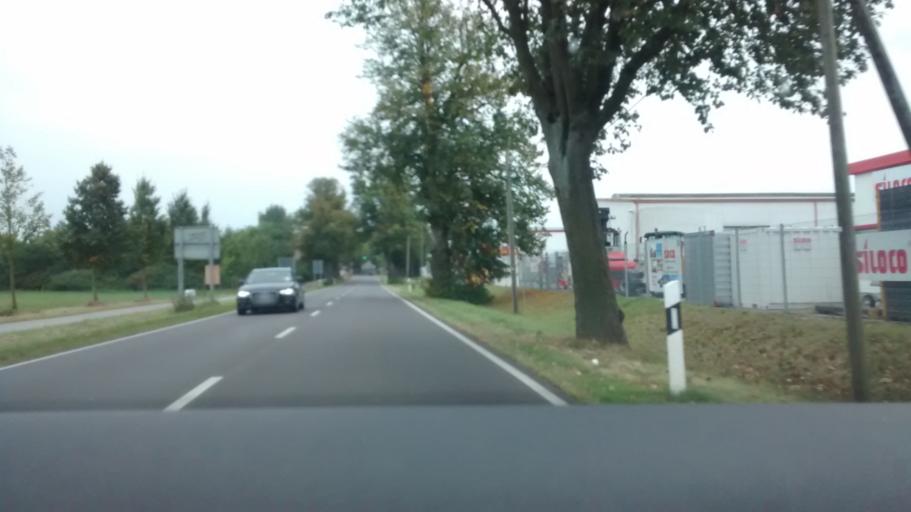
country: DE
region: Mecklenburg-Vorpommern
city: Wismar
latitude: 53.8678
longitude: 11.4506
